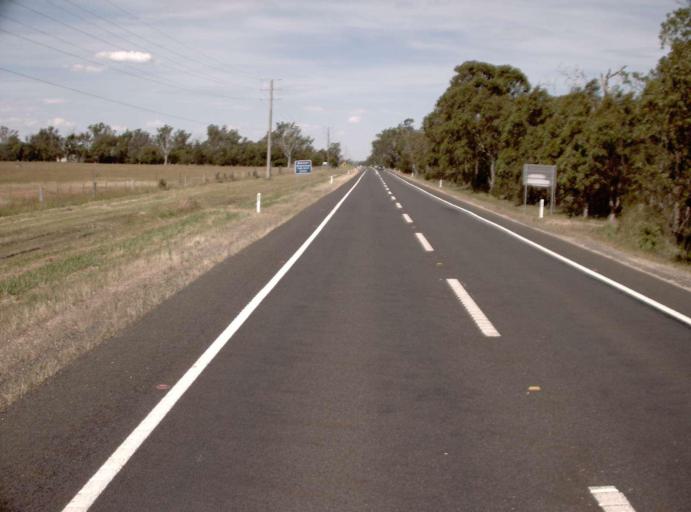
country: AU
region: Victoria
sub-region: East Gippsland
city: Bairnsdale
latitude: -37.8666
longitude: 147.4881
